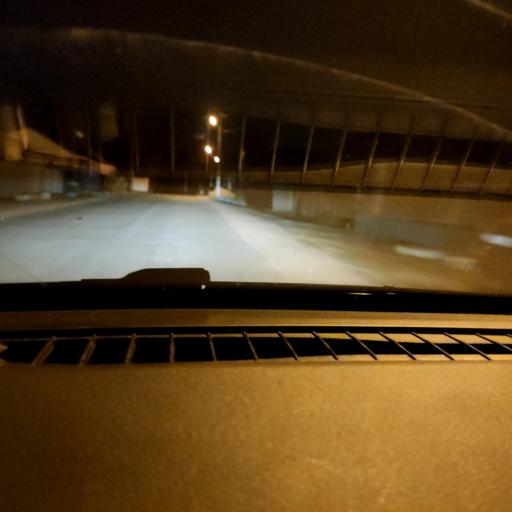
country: RU
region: Voronezj
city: Pridonskoy
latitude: 51.6667
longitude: 39.0835
